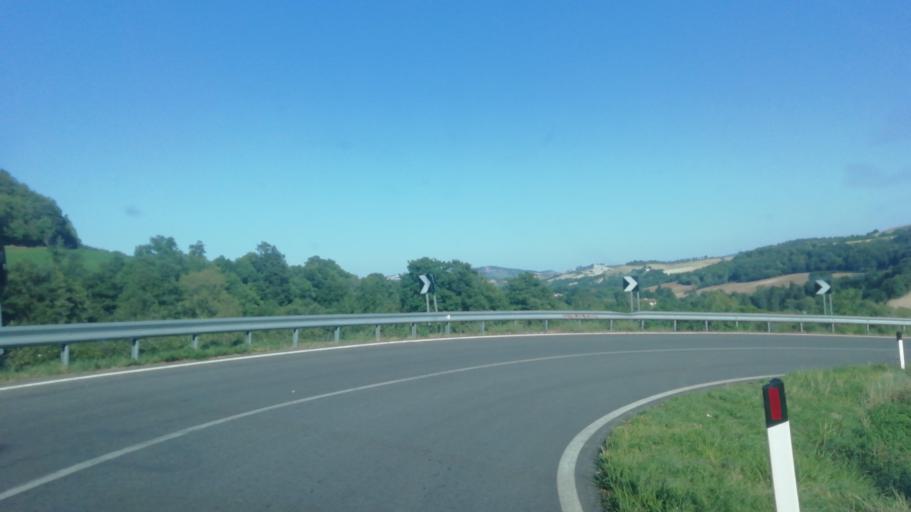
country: IT
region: The Marches
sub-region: Provincia di Pesaro e Urbino
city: Frontone
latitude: 43.5437
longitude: 12.7630
